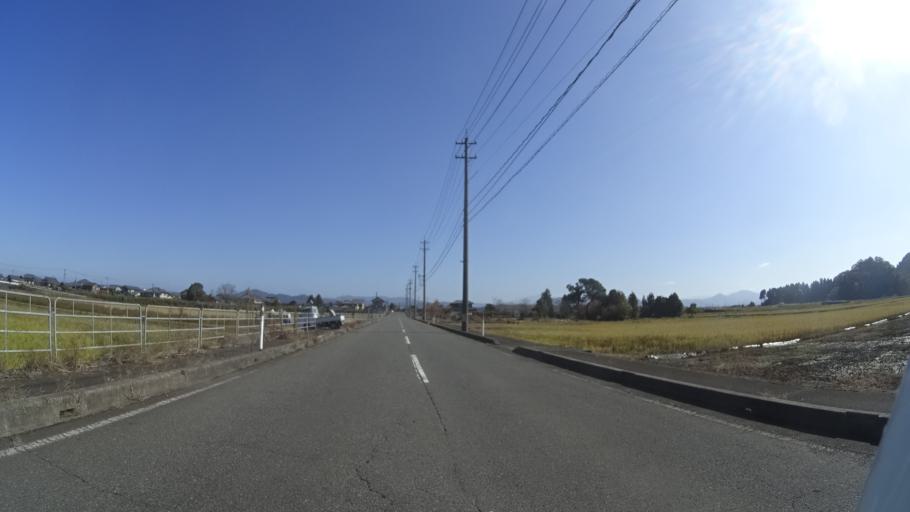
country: JP
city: Asahi
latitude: 35.9633
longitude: 136.1396
